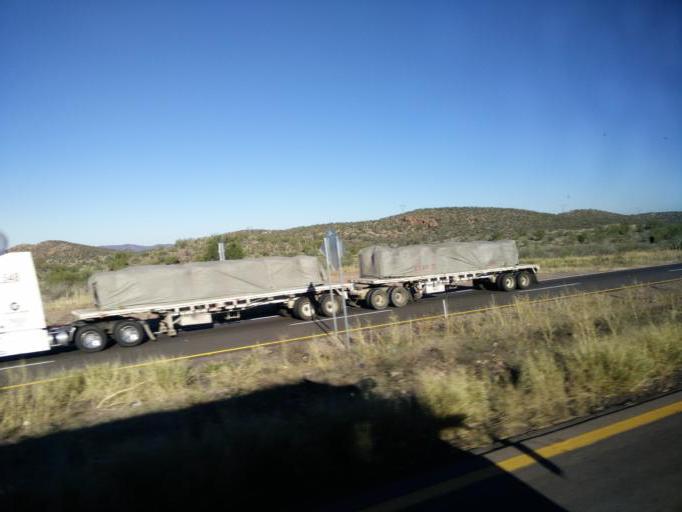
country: MX
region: Sonora
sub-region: Empalme
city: La Palma
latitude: 28.4685
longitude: -111.0478
